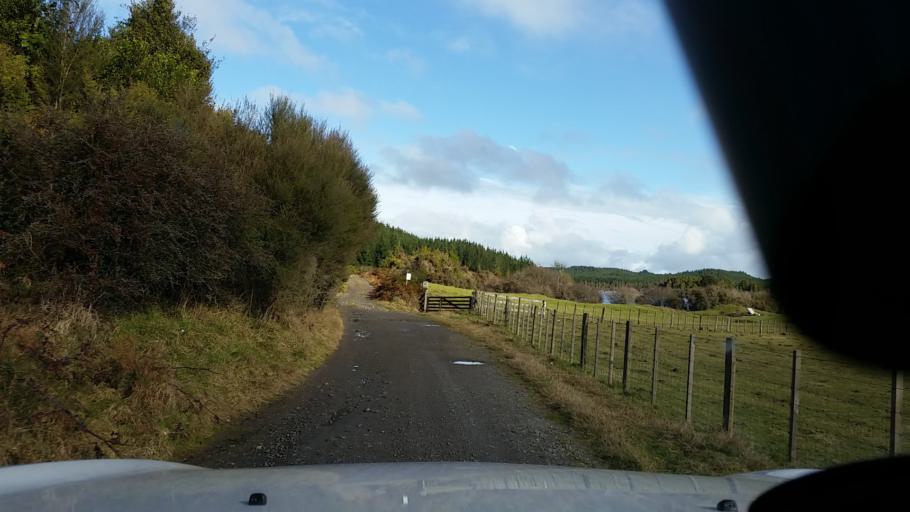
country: NZ
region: Bay of Plenty
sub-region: Rotorua District
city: Rotorua
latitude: -37.9895
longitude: 176.1628
